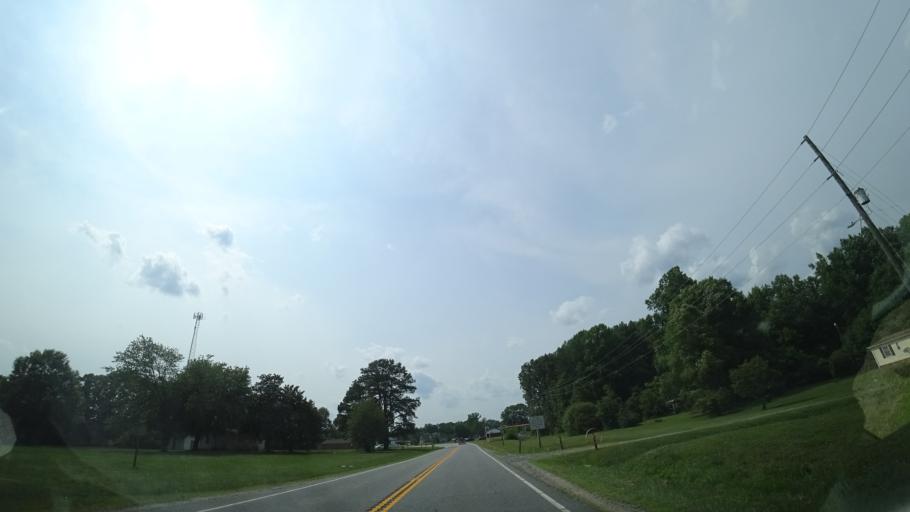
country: US
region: Virginia
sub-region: Spotsylvania County
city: Spotsylvania Courthouse
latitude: 38.1163
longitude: -77.7572
